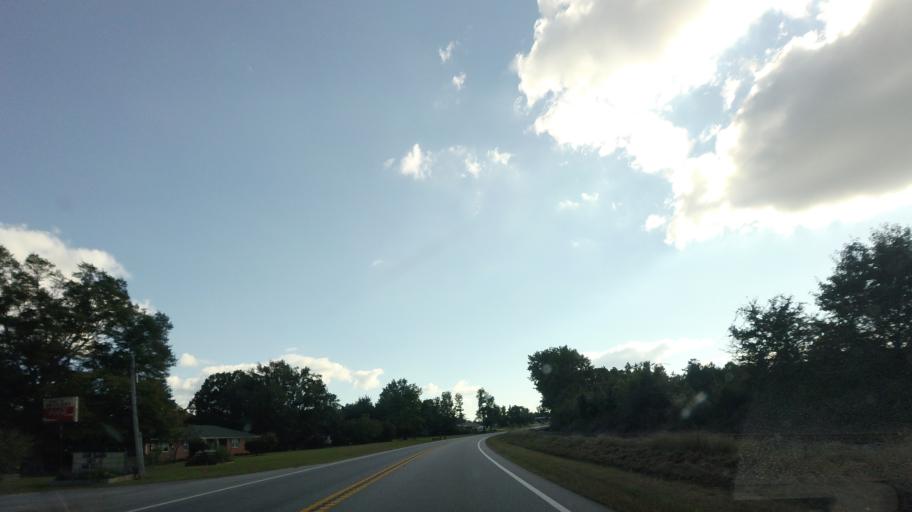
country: US
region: Georgia
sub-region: Lamar County
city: Barnesville
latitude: 33.0047
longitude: -84.1920
